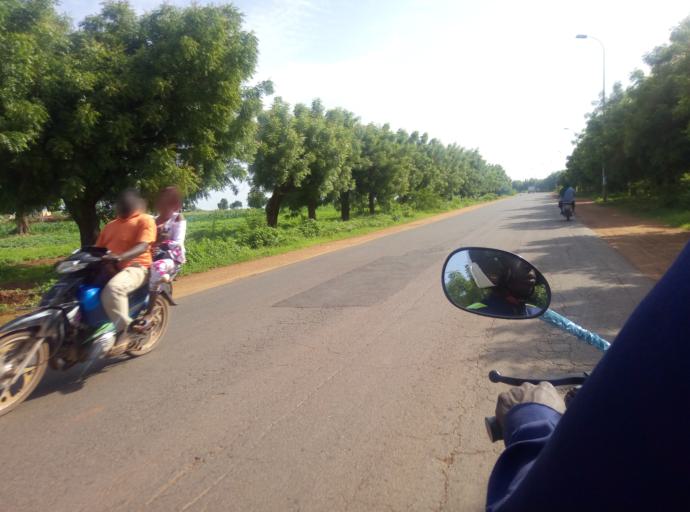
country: ML
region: Bamako
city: Bamako
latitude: 12.5550
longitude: -7.9453
